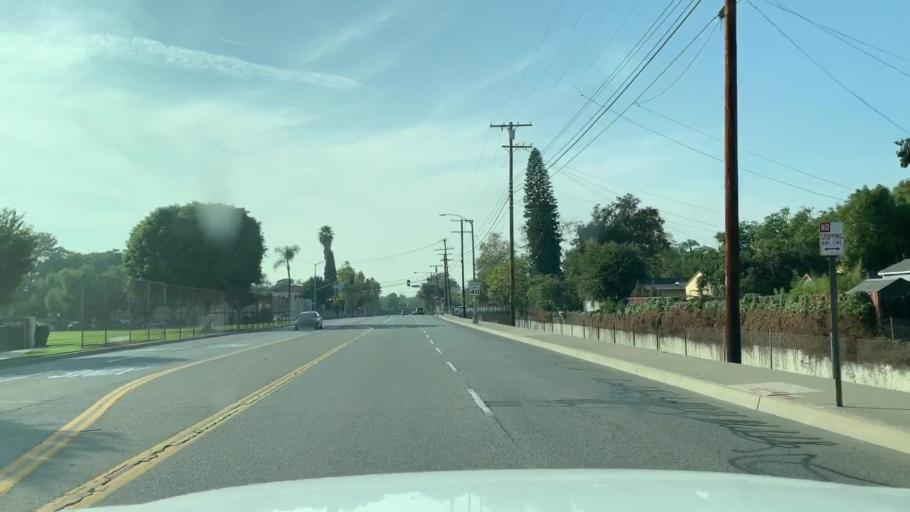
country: US
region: California
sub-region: Orange County
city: Fullerton
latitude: 33.8739
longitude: -117.9316
